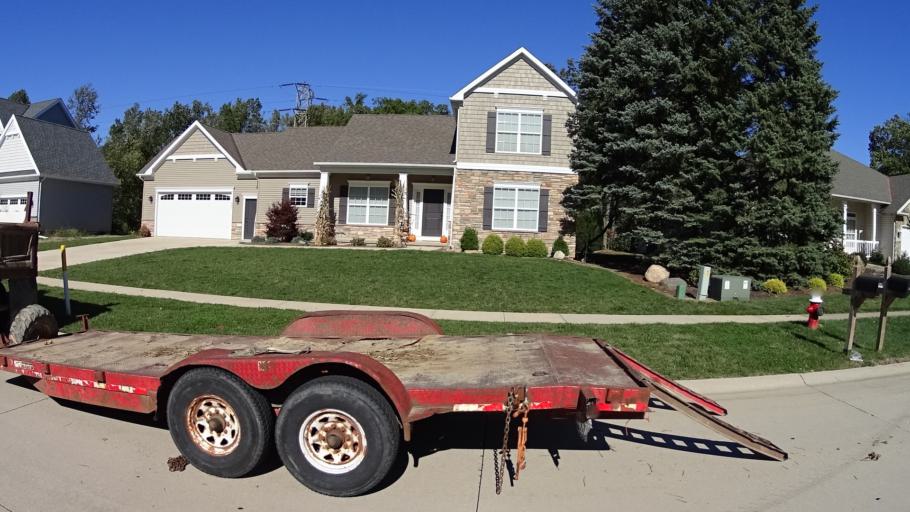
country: US
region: Ohio
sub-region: Lorain County
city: Amherst
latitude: 41.4026
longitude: -82.2519
